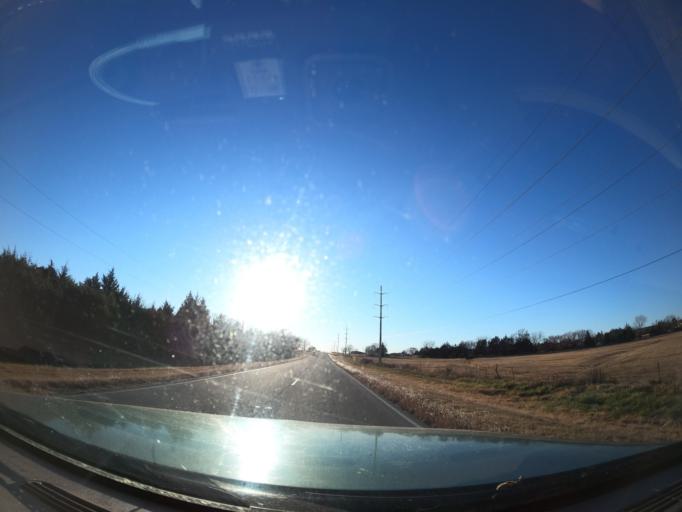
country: US
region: Oklahoma
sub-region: Pittsburg County
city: Hartshorne
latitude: 34.8801
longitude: -95.4999
